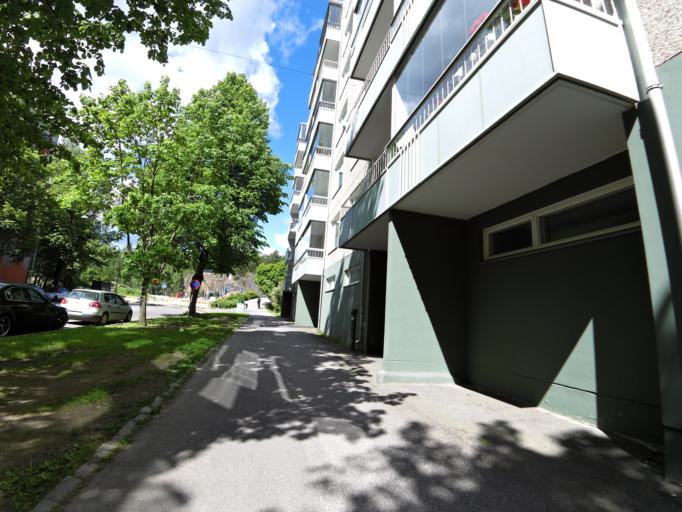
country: FI
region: Pirkanmaa
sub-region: Tampere
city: Tampere
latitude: 61.5061
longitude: 23.7794
